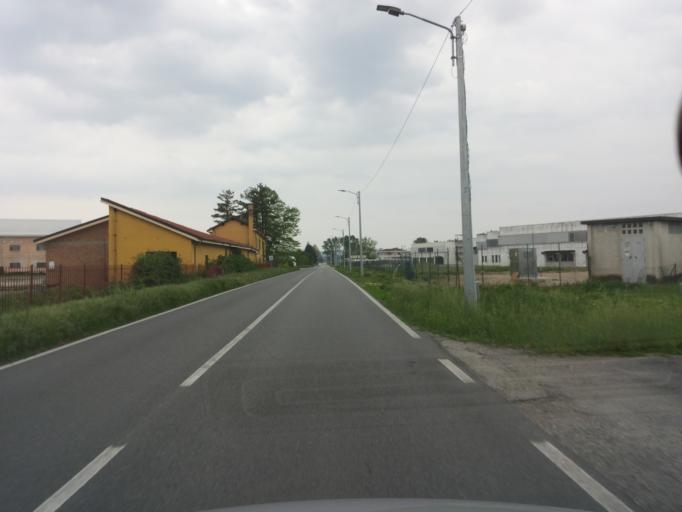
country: IT
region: Piedmont
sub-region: Provincia di Alessandria
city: Occimiano
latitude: 45.0703
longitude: 8.4925
